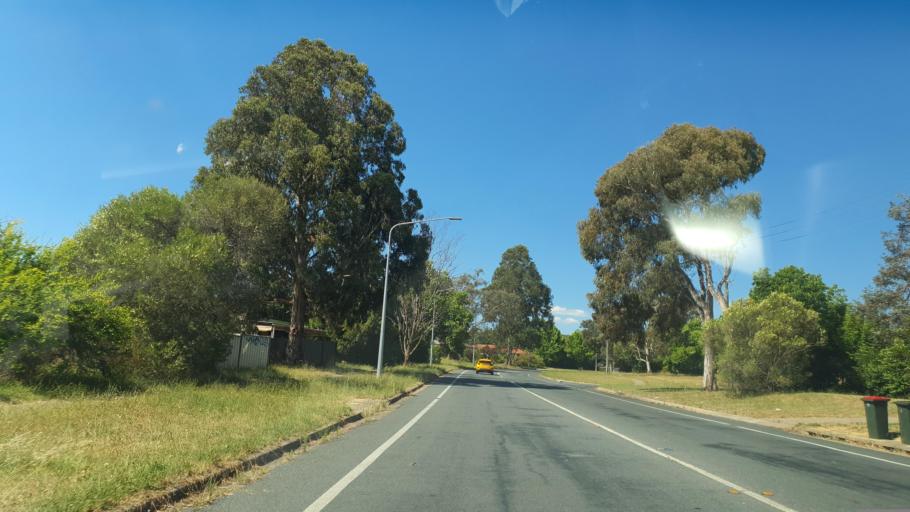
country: AU
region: Australian Capital Territory
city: Belconnen
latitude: -35.2039
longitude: 149.0393
